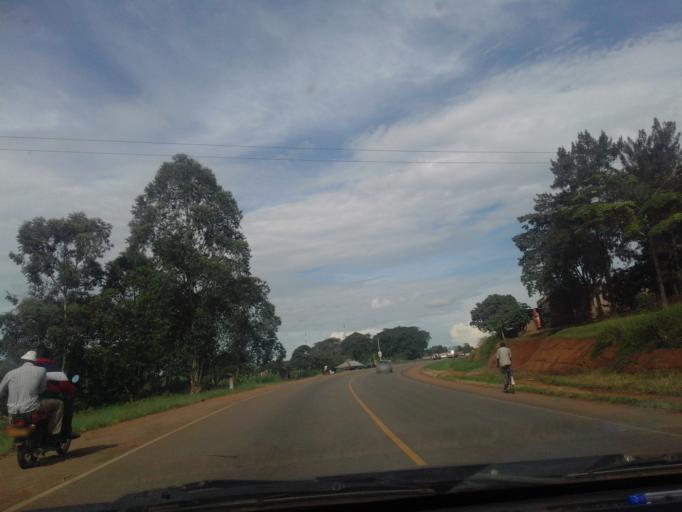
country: UG
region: Central Region
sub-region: Lwengo District
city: Lwengo
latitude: -0.3554
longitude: 31.5472
